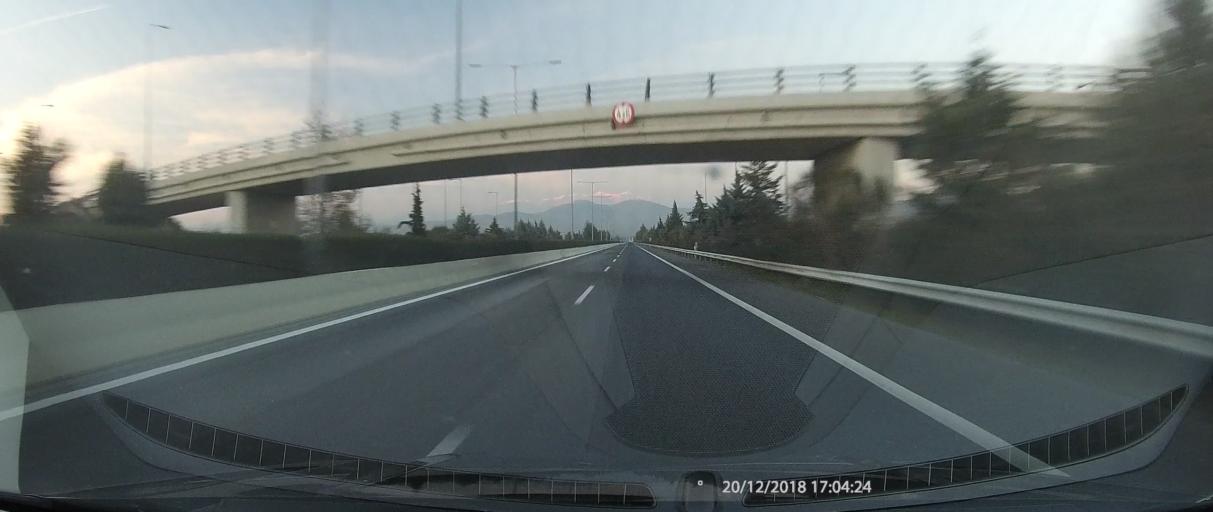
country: GR
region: Thessaly
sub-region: Nomos Larisis
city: Makrychori
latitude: 39.7169
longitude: 22.4824
